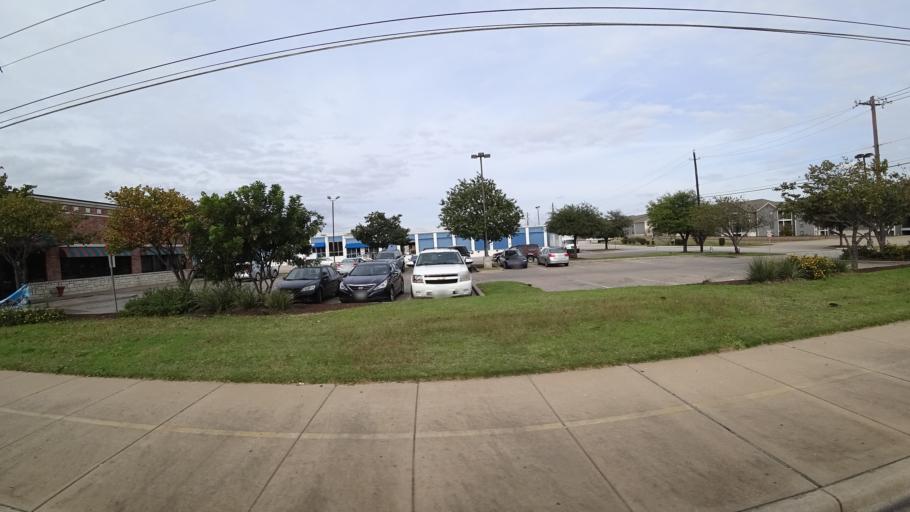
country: US
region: Texas
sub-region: Travis County
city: Wells Branch
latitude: 30.4237
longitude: -97.6694
